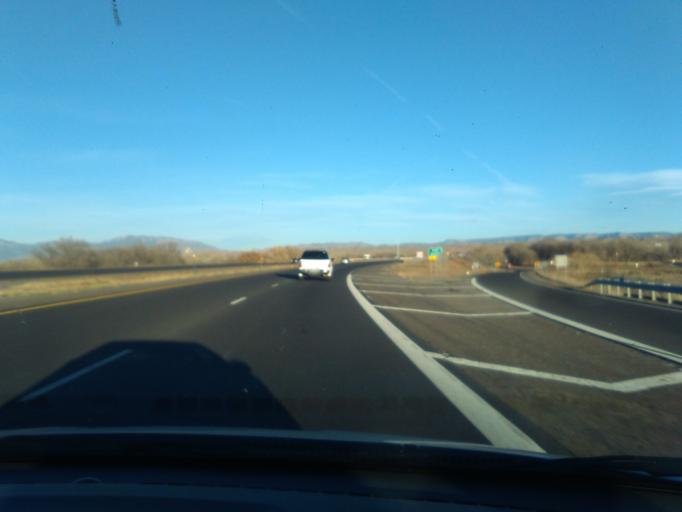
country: US
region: New Mexico
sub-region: Bernalillo County
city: South Valley
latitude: 34.9476
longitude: -106.6973
